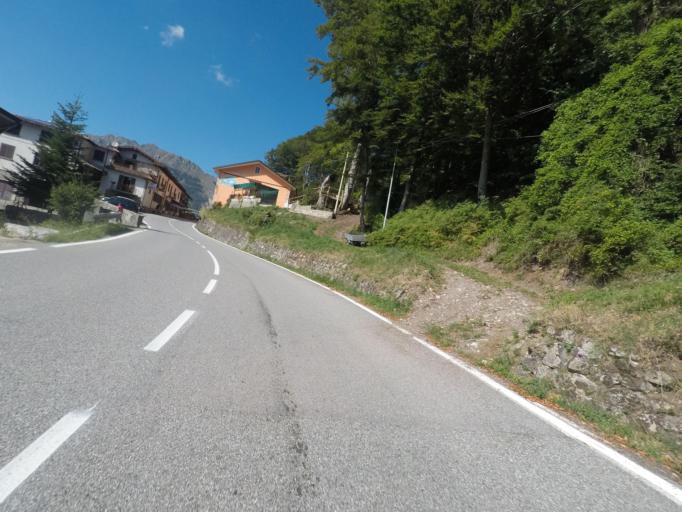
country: IT
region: Tuscany
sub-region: Provincia di Massa-Carrara
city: Comano
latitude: 44.2823
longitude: 10.1984
